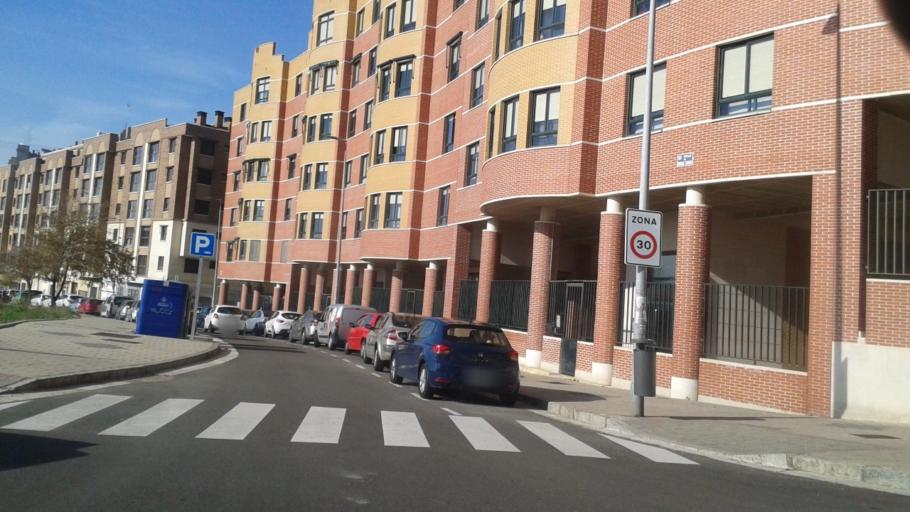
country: ES
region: Castille and Leon
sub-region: Provincia de Valladolid
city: Zaratan
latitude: 41.6352
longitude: -4.7619
